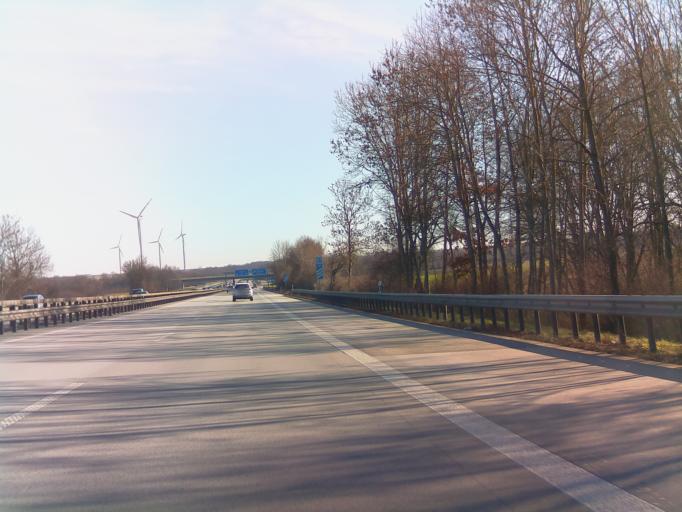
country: DE
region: Rheinland-Pfalz
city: Morstadt
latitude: 49.6728
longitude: 8.2628
